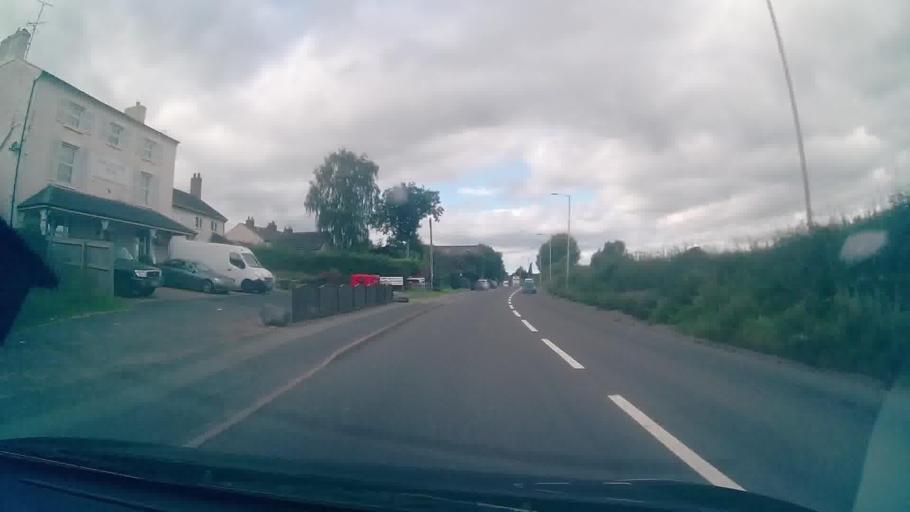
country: GB
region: England
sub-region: Shropshire
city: Whitchurch
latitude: 52.9806
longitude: -2.7087
